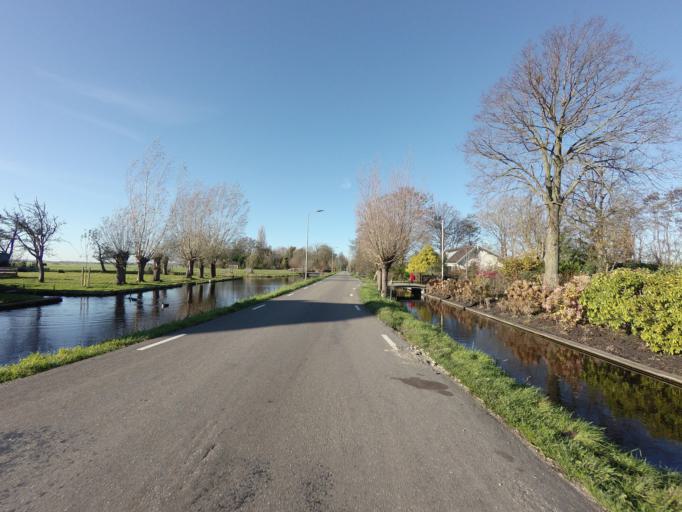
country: NL
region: South Holland
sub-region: Gemeente Nieuwkoop
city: Nieuwkoop
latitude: 52.1310
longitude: 4.7490
